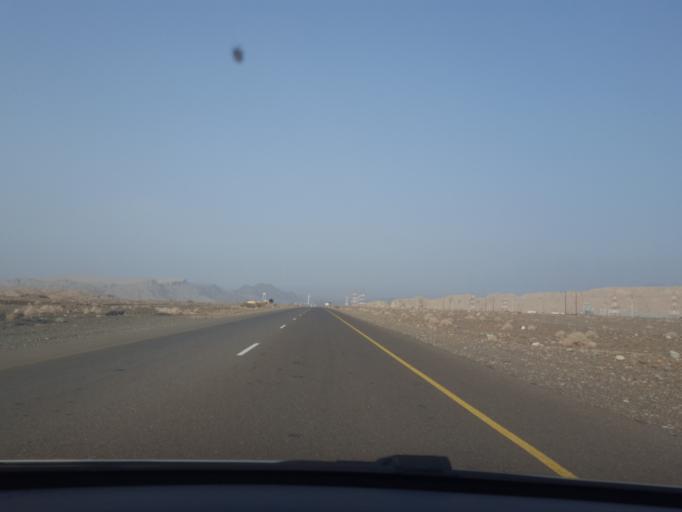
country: AE
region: Abu Dhabi
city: Al Ain
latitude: 24.0328
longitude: 56.0010
